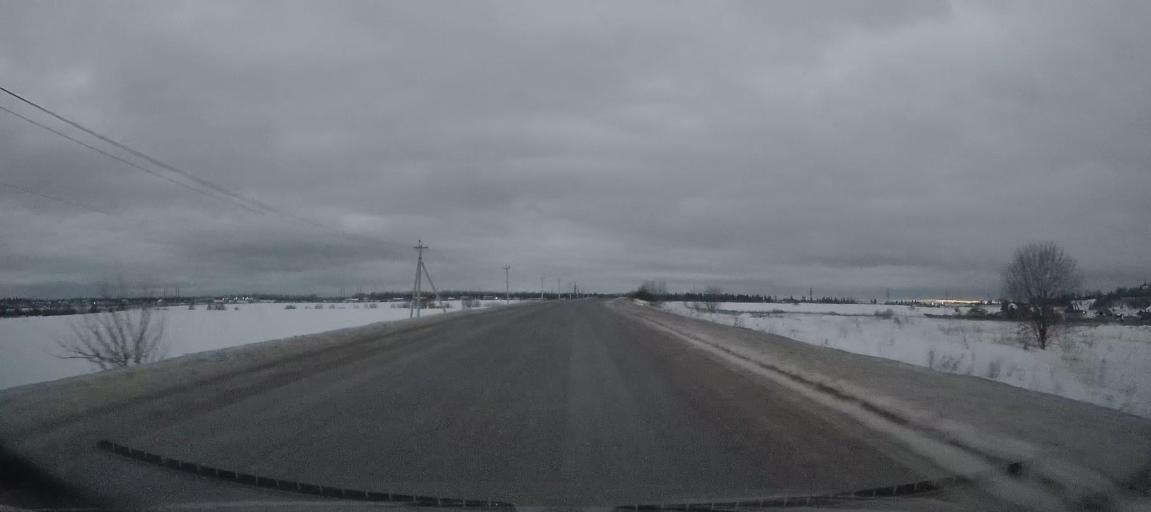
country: RU
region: Leningrad
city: Taytsy
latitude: 59.6883
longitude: 30.1336
